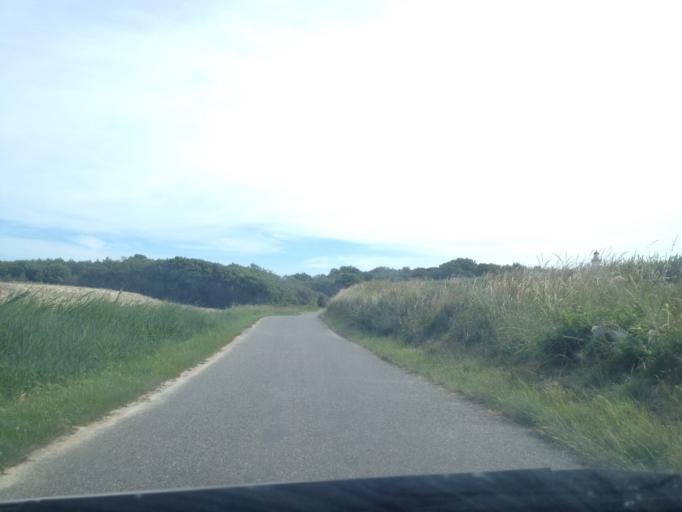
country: DK
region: Central Jutland
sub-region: Samso Kommune
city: Tranebjerg
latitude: 55.7734
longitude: 10.5517
